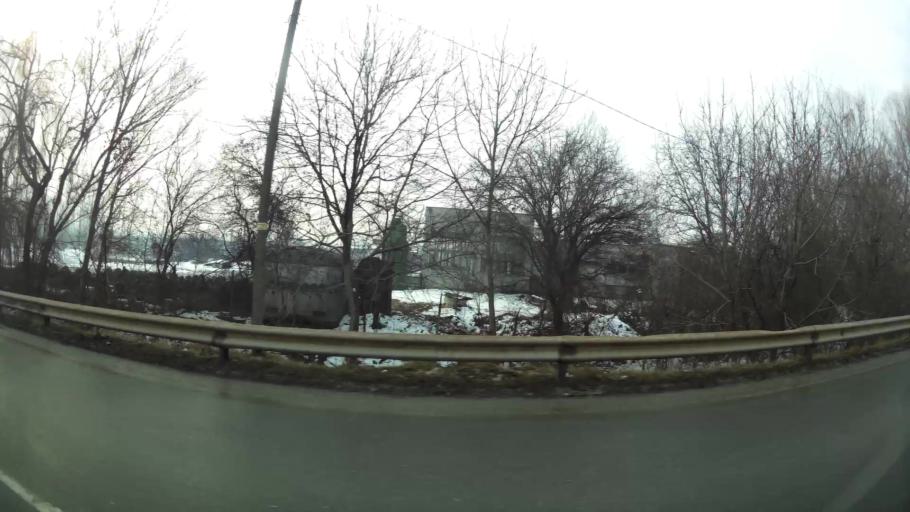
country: MK
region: Ilinden
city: Jurumleri
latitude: 41.9748
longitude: 21.5371
